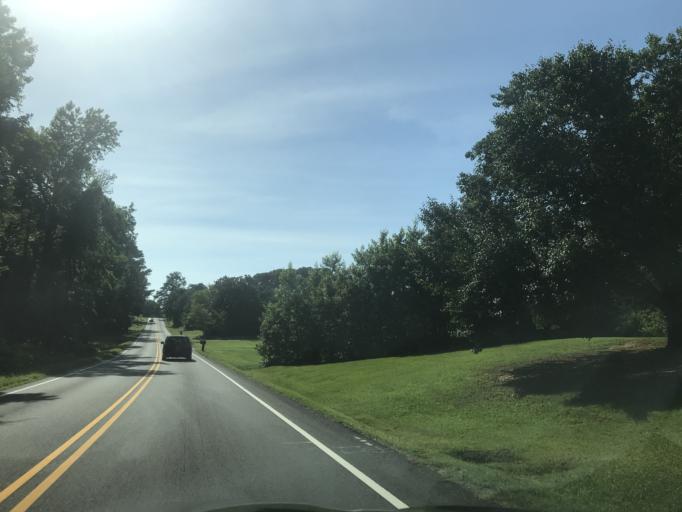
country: US
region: North Carolina
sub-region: Wake County
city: Garner
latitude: 35.6617
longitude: -78.5482
